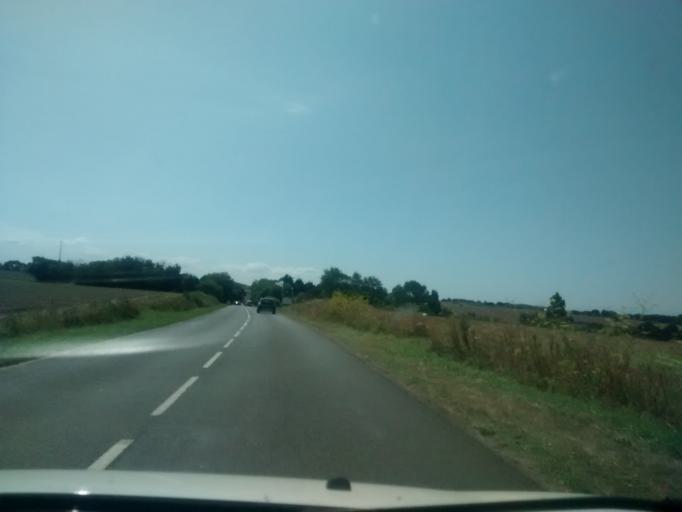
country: FR
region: Brittany
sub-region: Departement d'Ille-et-Vilaine
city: Cancale
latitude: 48.6914
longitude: -1.8726
